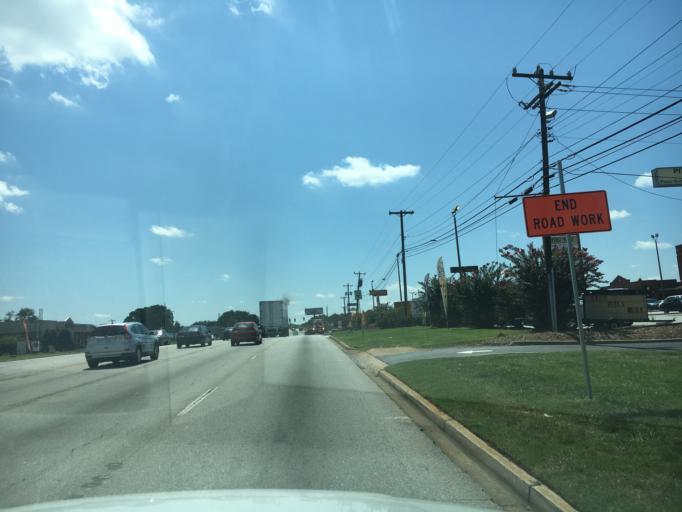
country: US
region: South Carolina
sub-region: Greenville County
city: Wade Hampton
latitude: 34.9162
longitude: -82.3181
